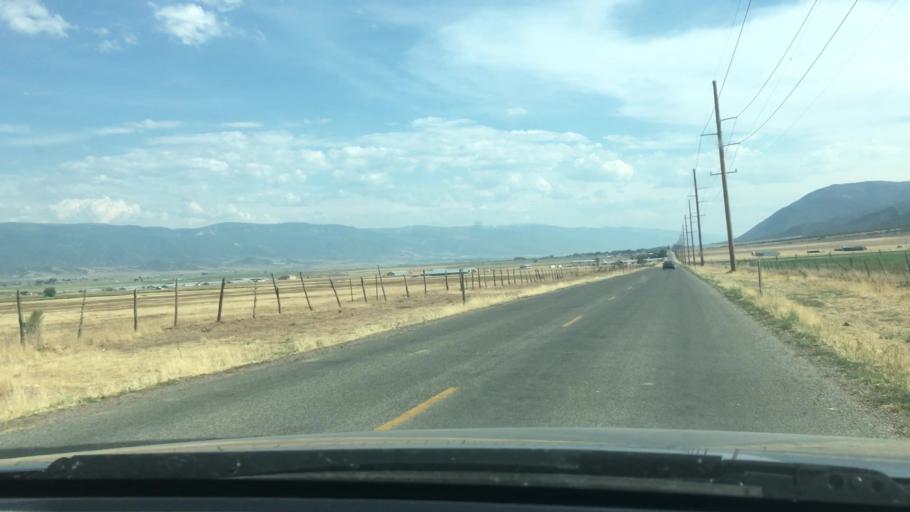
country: US
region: Utah
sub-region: Sanpete County
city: Moroni
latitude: 39.5399
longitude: -111.6400
